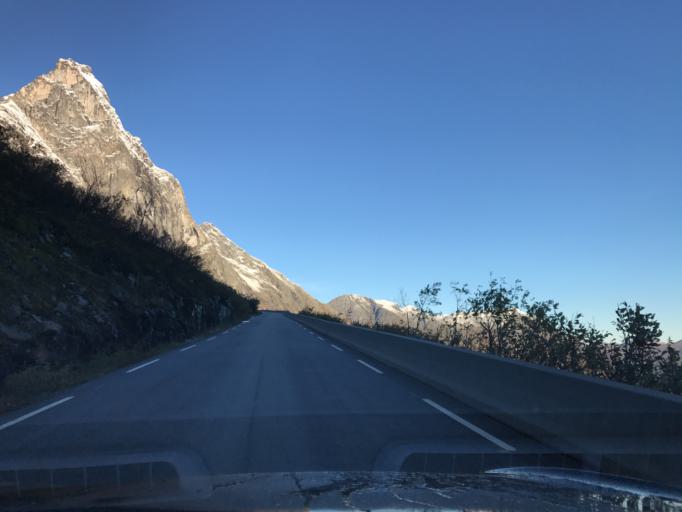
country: NO
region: More og Romsdal
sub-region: Rauma
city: Andalsnes
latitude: 62.4602
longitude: 7.6681
